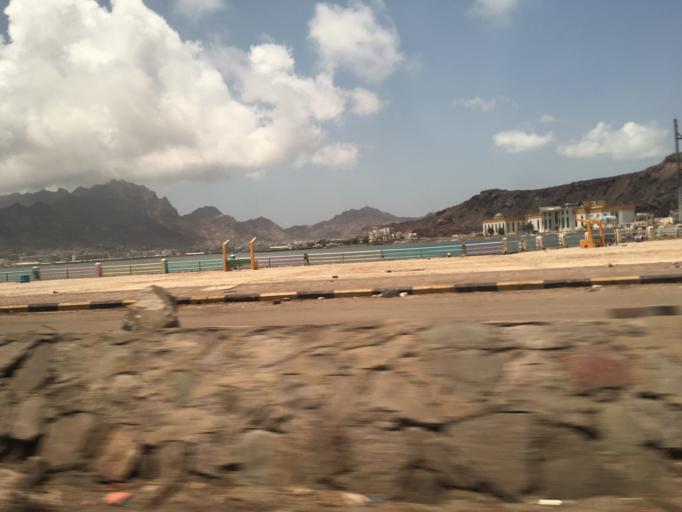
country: YE
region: Aden
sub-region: Khur Maksar
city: Khawr Maksar
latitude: 12.8104
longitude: 45.0242
